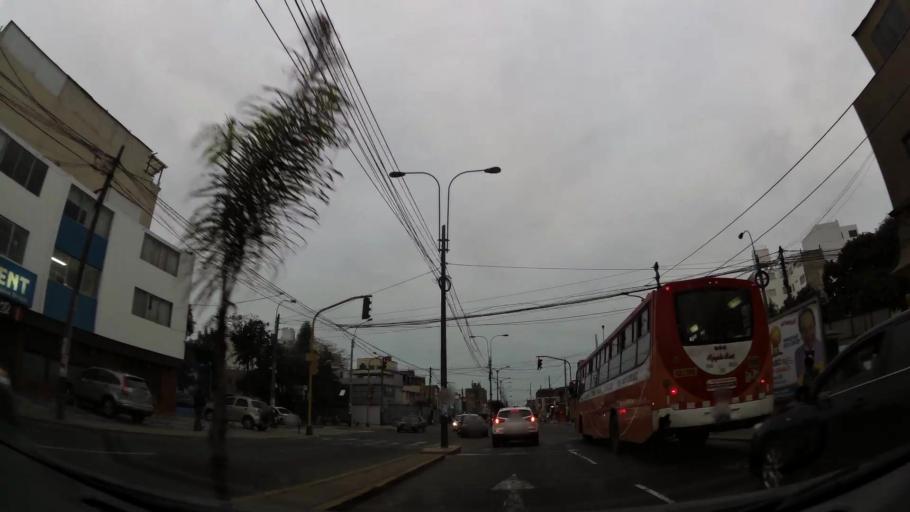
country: PE
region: Lima
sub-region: Lima
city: San Isidro
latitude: -12.0735
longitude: -77.0623
